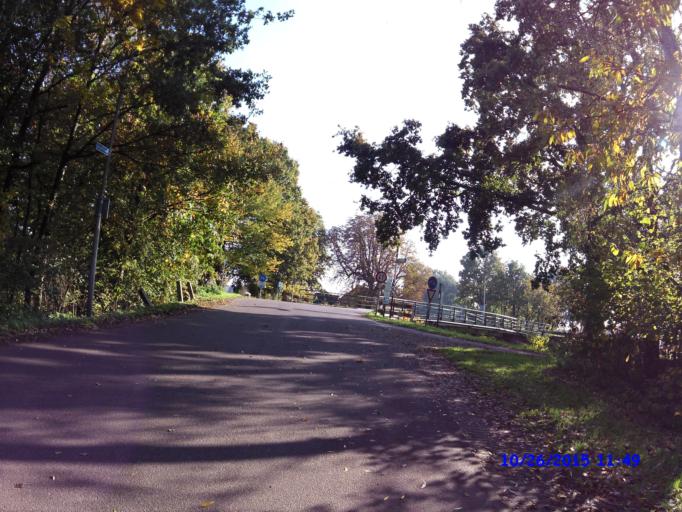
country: NL
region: North Brabant
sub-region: Gemeente Geldrop-Mierlo
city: Mierlo
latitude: 51.4482
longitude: 5.6031
